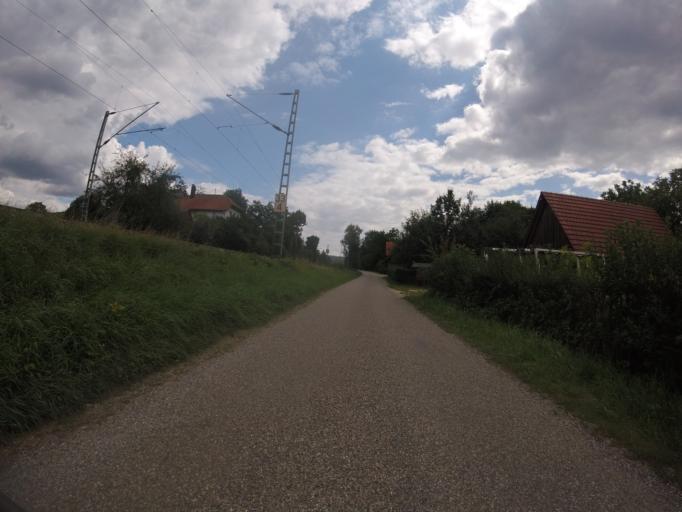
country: DE
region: Baden-Wuerttemberg
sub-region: Regierungsbezirk Stuttgart
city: Pluderhausen
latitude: 48.7878
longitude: 9.6108
